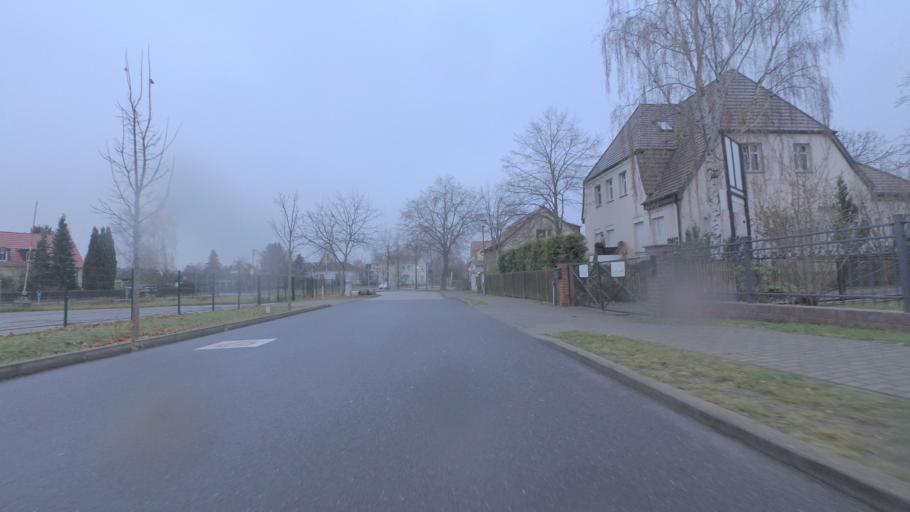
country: DE
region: Brandenburg
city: Grossbeeren
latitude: 52.3526
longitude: 13.3038
